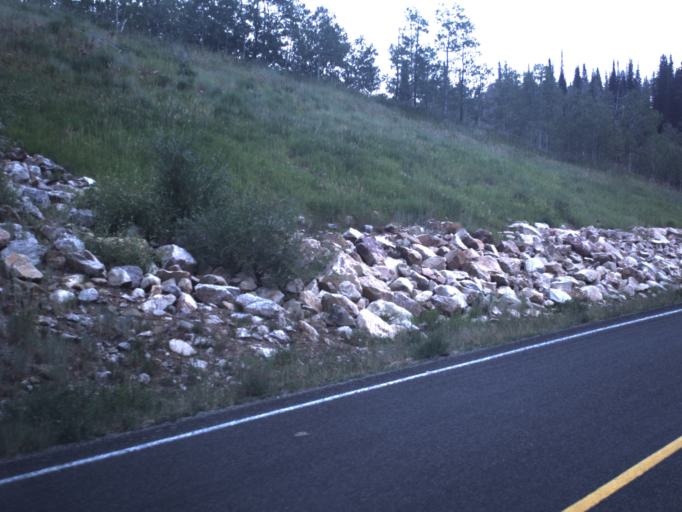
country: US
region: Utah
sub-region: Summit County
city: Francis
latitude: 40.5244
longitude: -111.0922
